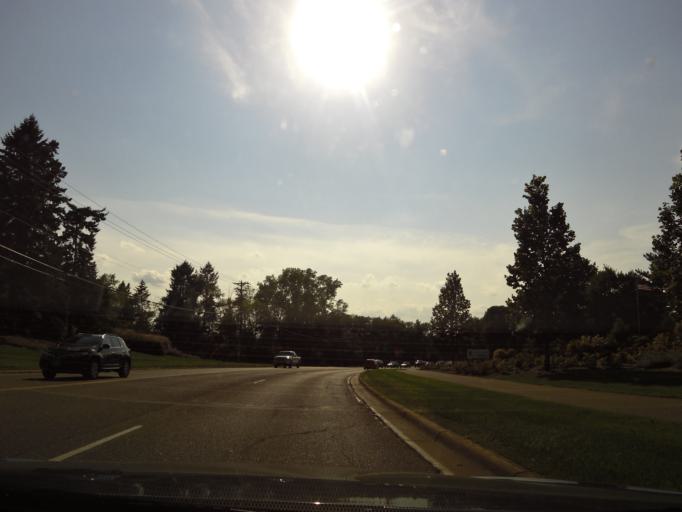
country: US
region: Minnesota
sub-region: Washington County
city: Newport
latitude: 44.8888
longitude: -92.9907
